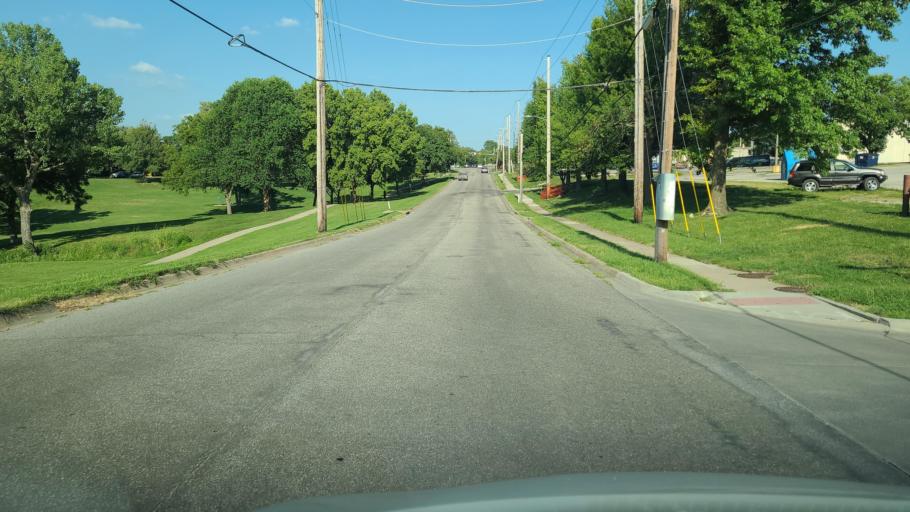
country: US
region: Kansas
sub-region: Douglas County
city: Lawrence
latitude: 38.9679
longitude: -95.2640
